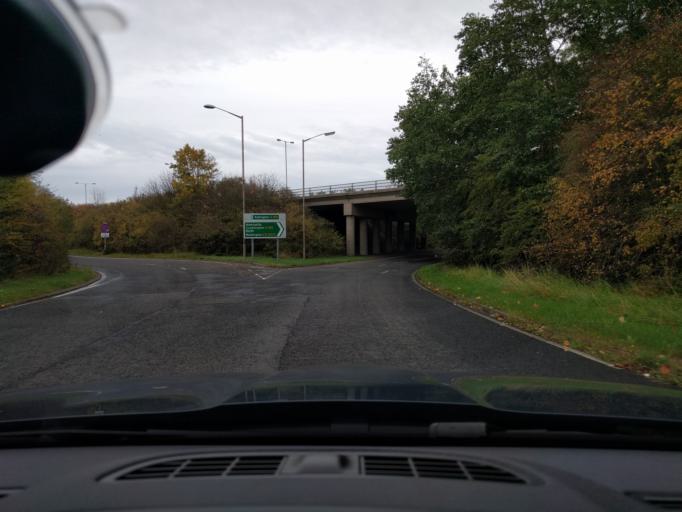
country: GB
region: England
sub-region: Northumberland
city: Bedlington
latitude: 55.1399
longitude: -1.5592
